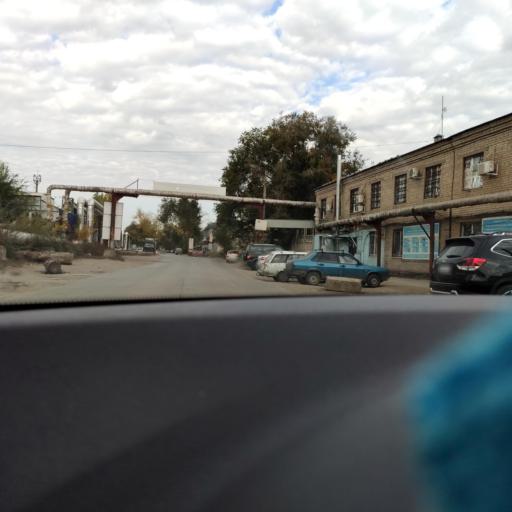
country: RU
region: Samara
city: Samara
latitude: 53.1952
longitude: 50.2609
